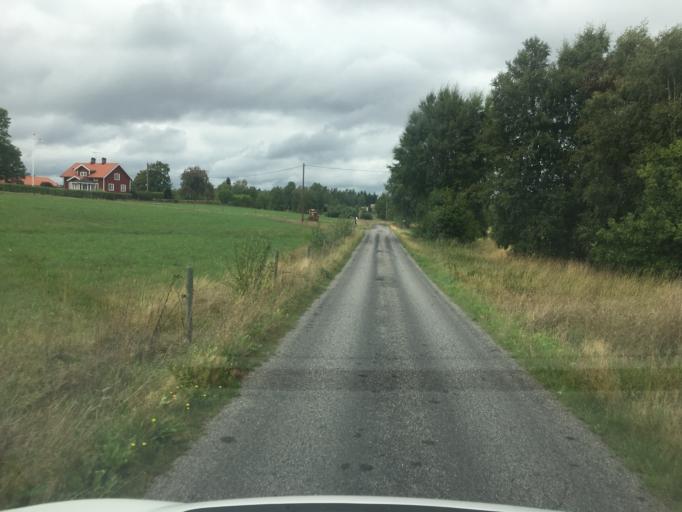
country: SE
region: Kronoberg
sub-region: Ljungby Kommun
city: Lagan
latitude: 56.9294
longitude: 14.0257
